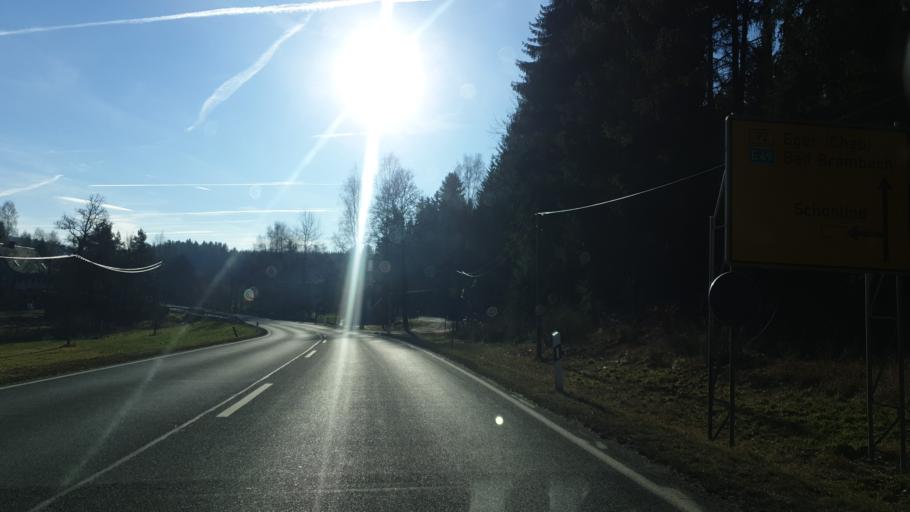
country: DE
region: Saxony
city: Markneukirchen
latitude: 50.2744
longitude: 12.2934
